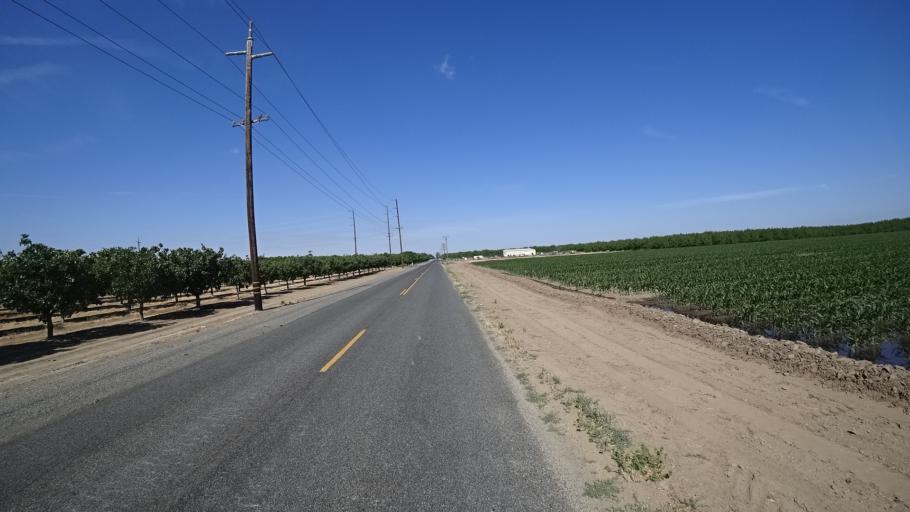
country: US
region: California
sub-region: Kings County
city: Armona
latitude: 36.2548
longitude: -119.6894
